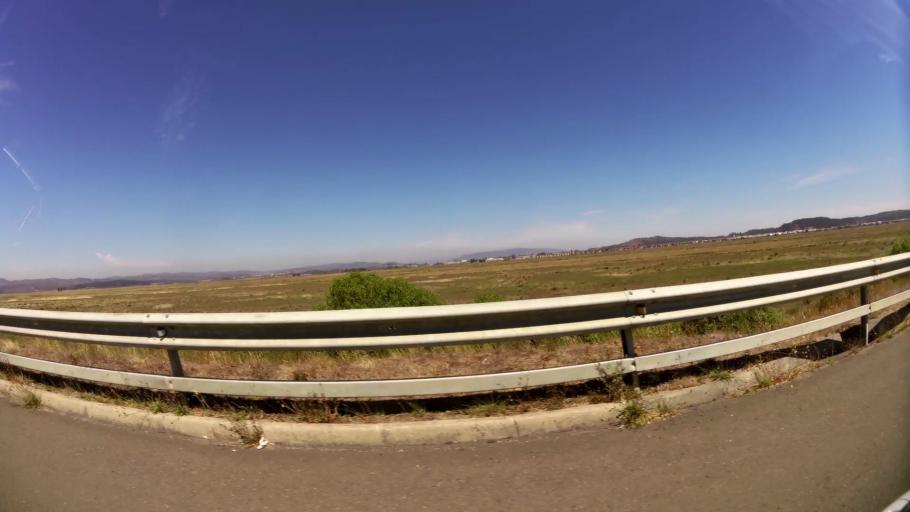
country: CL
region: Biobio
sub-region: Provincia de Concepcion
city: Talcahuano
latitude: -36.7339
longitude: -73.0768
